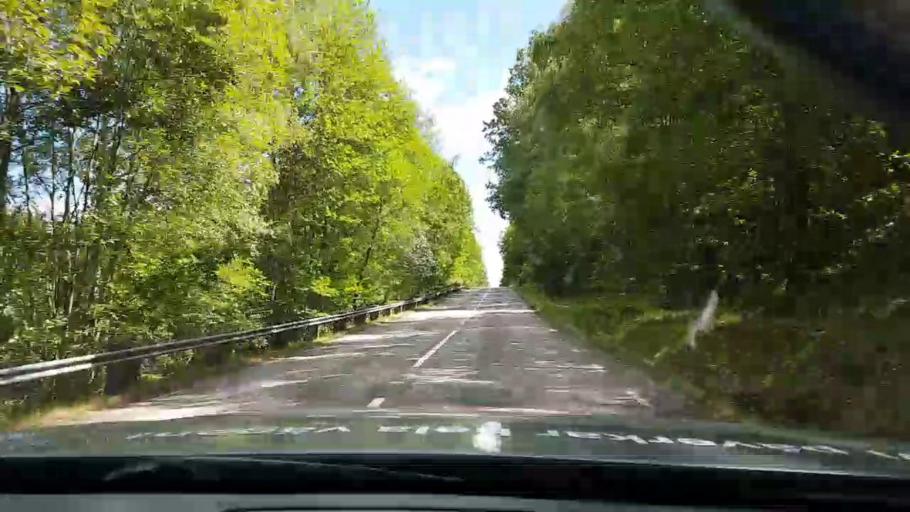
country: SE
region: Kalmar
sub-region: Vasterviks Kommun
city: Overum
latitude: 58.0708
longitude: 16.3814
